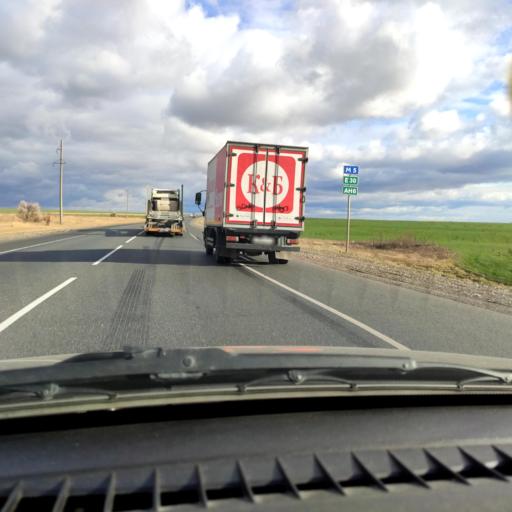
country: RU
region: Samara
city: Varlamovo
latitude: 53.2068
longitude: 48.3867
